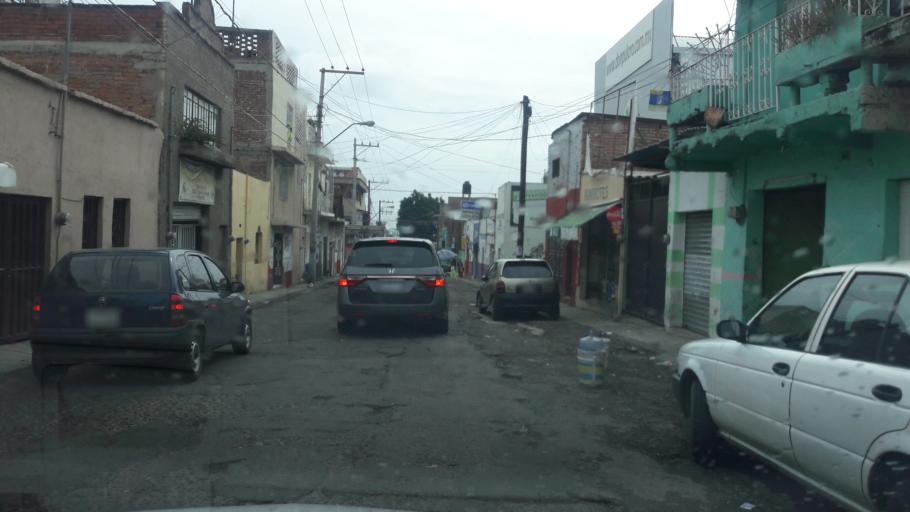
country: MX
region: Guanajuato
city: Leon
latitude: 21.1189
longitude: -101.6895
